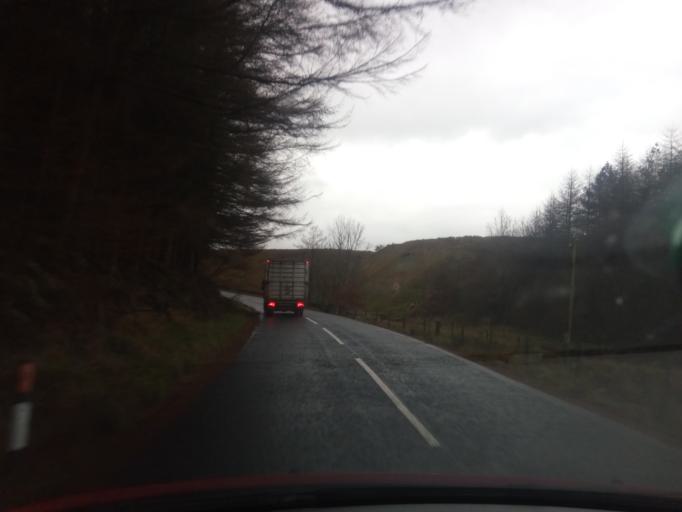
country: GB
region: Scotland
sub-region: The Scottish Borders
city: Hawick
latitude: 55.2709
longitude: -2.6899
